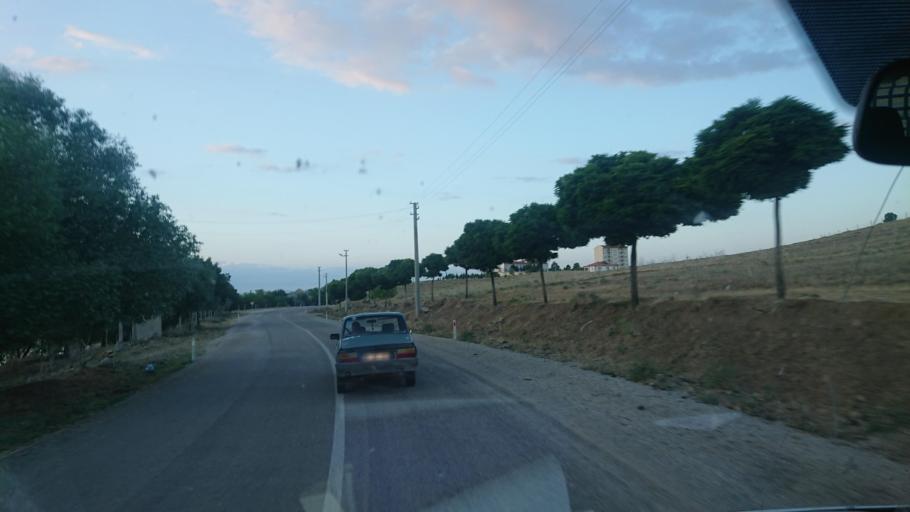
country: TR
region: Aksaray
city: Sariyahsi
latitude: 38.9694
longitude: 33.8286
